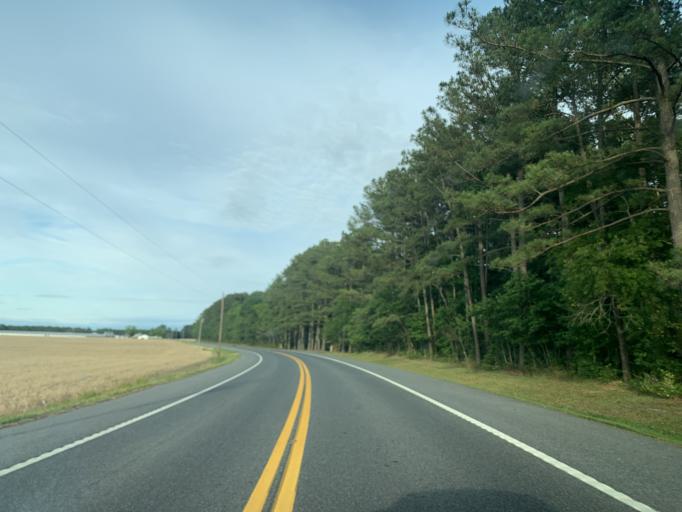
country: US
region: Virginia
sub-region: Accomack County
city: Captains Cove
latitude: 38.0684
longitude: -75.4630
